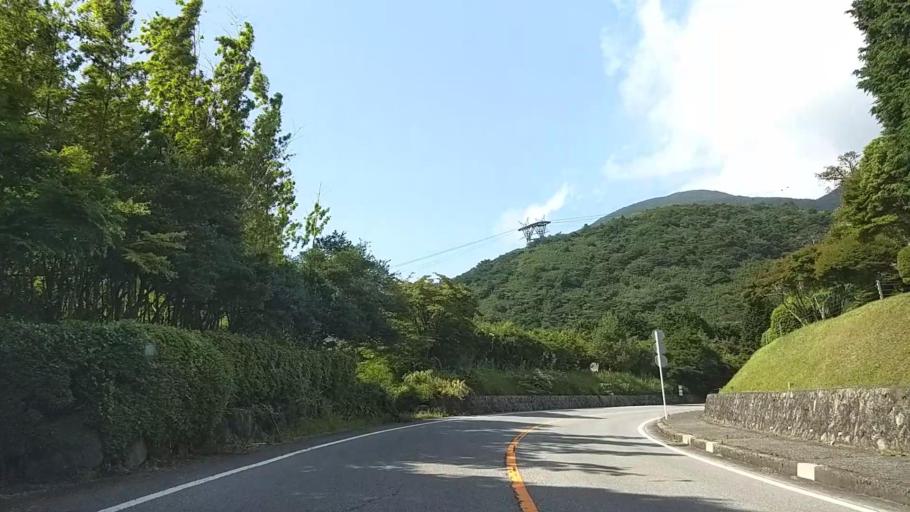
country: JP
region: Kanagawa
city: Hakone
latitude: 35.2129
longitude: 139.0145
